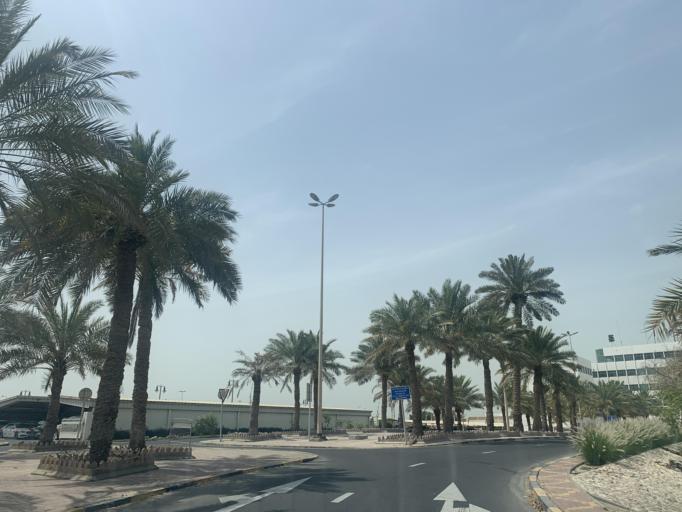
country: BH
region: Northern
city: Madinat `Isa
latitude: 26.1550
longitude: 50.5387
